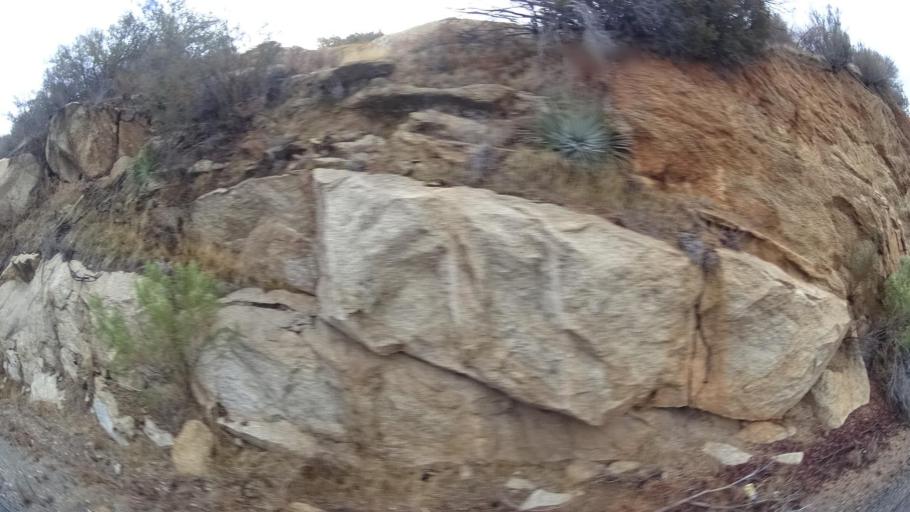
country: MX
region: Baja California
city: Tecate
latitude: 32.6046
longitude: -116.6336
